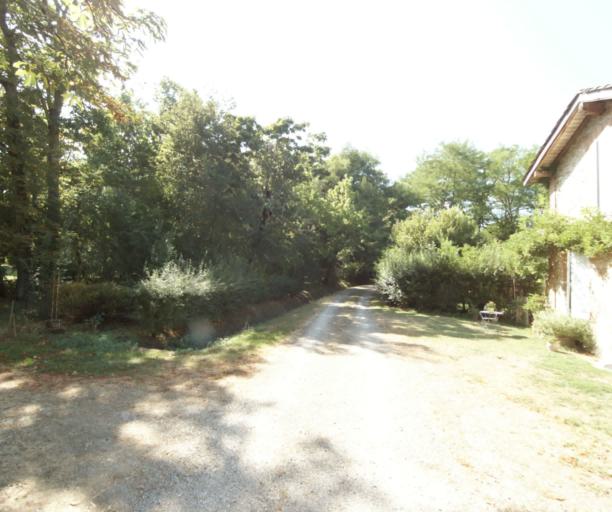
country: FR
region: Midi-Pyrenees
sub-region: Departement de la Haute-Garonne
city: Revel
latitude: 43.5072
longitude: 1.9816
